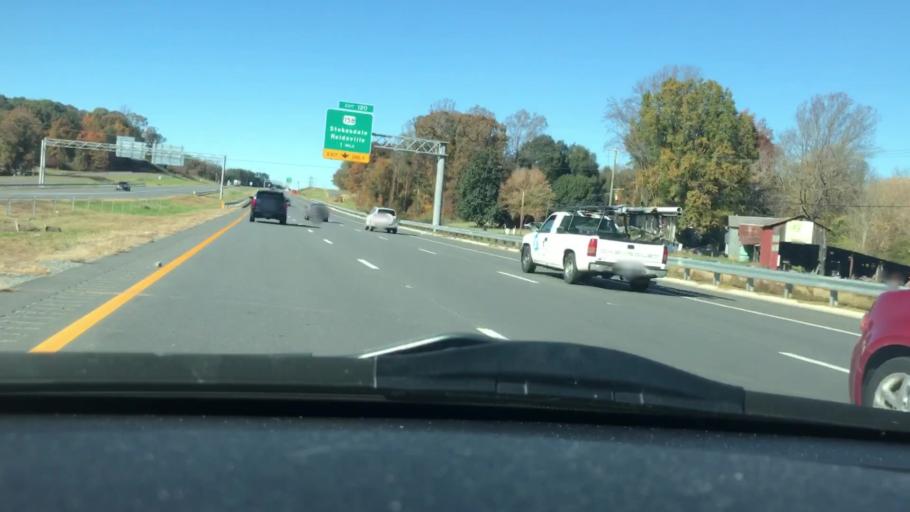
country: US
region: North Carolina
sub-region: Guilford County
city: Summerfield
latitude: 36.2298
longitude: -79.9146
